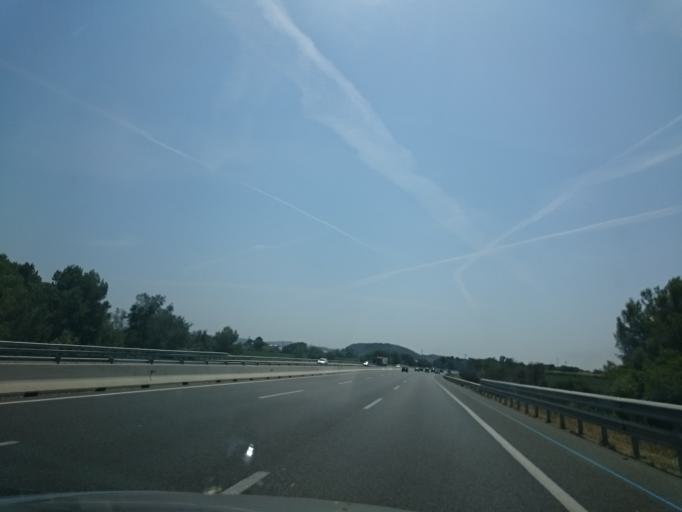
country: ES
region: Catalonia
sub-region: Provincia de Barcelona
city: Castellet
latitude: 41.3200
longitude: 1.6398
